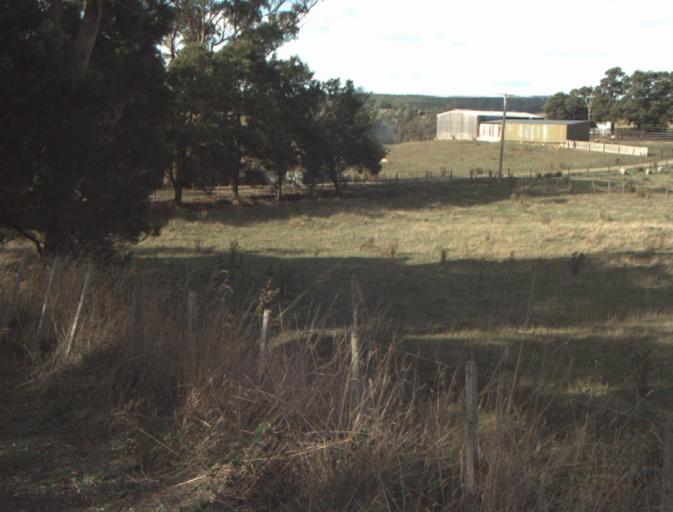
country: AU
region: Tasmania
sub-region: Launceston
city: Mayfield
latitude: -41.2086
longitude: 147.1070
